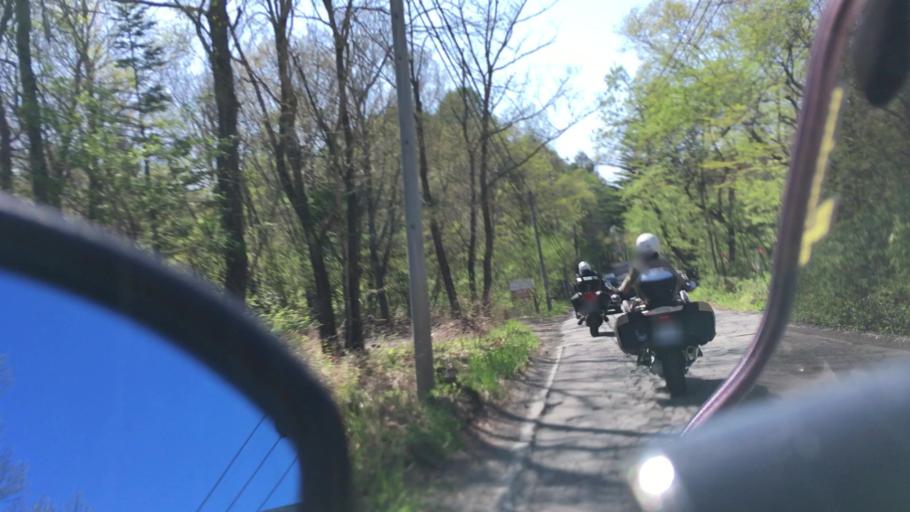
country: JP
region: Nagano
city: Komoro
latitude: 36.4644
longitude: 138.5496
